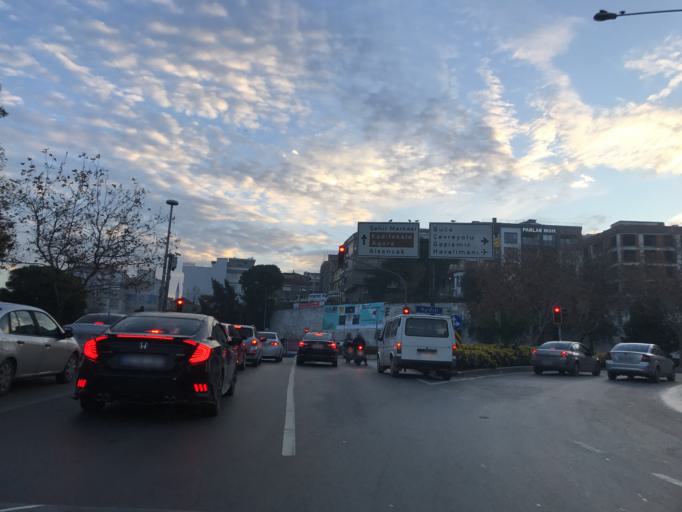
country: TR
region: Izmir
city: Izmir
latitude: 38.4059
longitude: 27.1215
